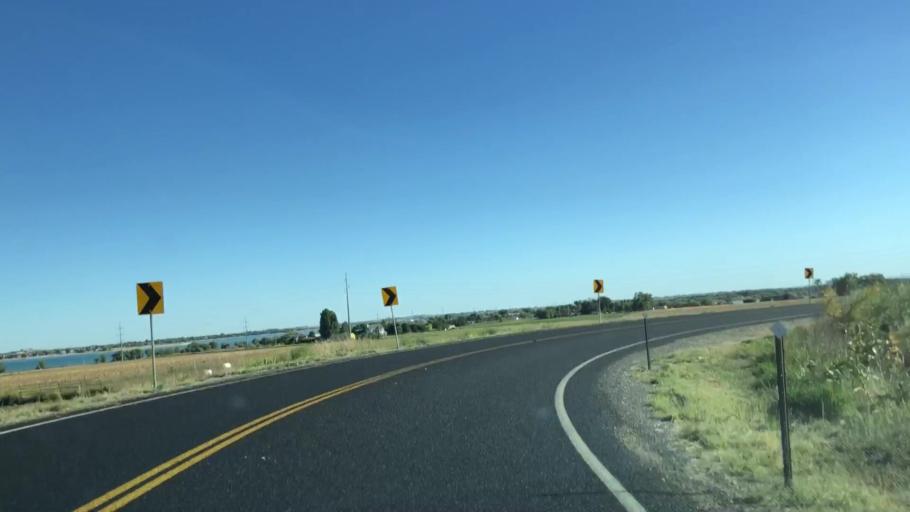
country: US
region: Colorado
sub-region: Larimer County
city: Loveland
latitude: 40.4617
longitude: -105.0495
